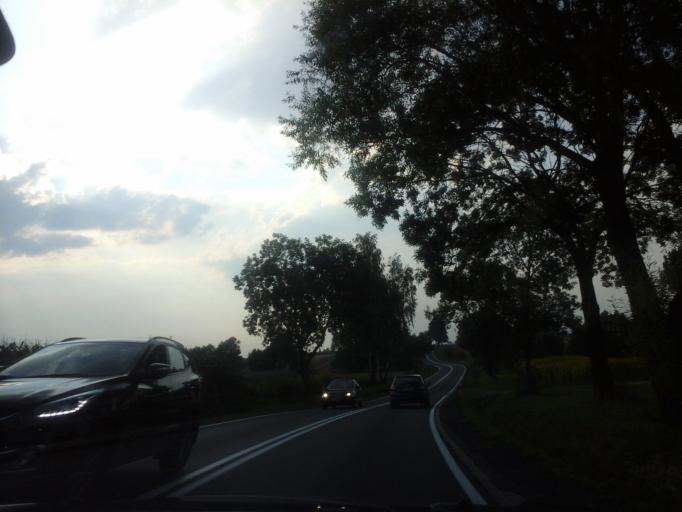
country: PL
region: Lesser Poland Voivodeship
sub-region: Powiat wadowicki
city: Spytkowice
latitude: 49.9886
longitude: 19.5240
